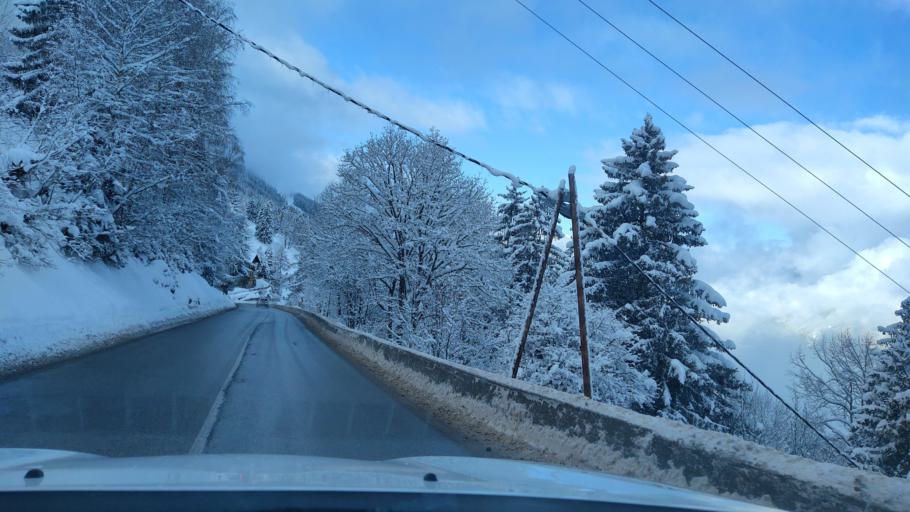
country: FR
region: Rhone-Alpes
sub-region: Departement de la Savoie
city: Saint-Bon-Tarentaise
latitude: 45.4276
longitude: 6.6389
